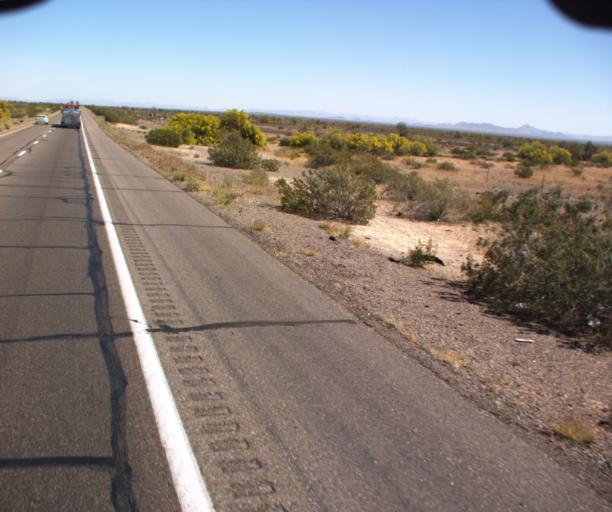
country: US
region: Arizona
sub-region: Maricopa County
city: Gila Bend
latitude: 32.8912
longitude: -113.0551
